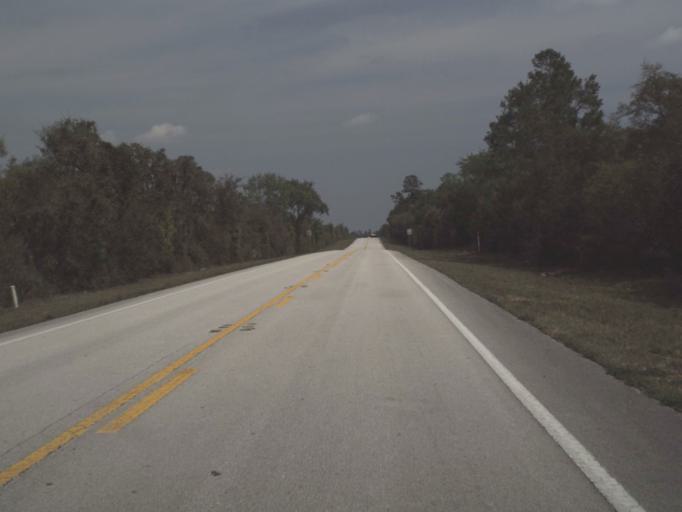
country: US
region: Florida
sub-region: Lake County
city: Astor
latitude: 29.2232
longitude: -81.6461
